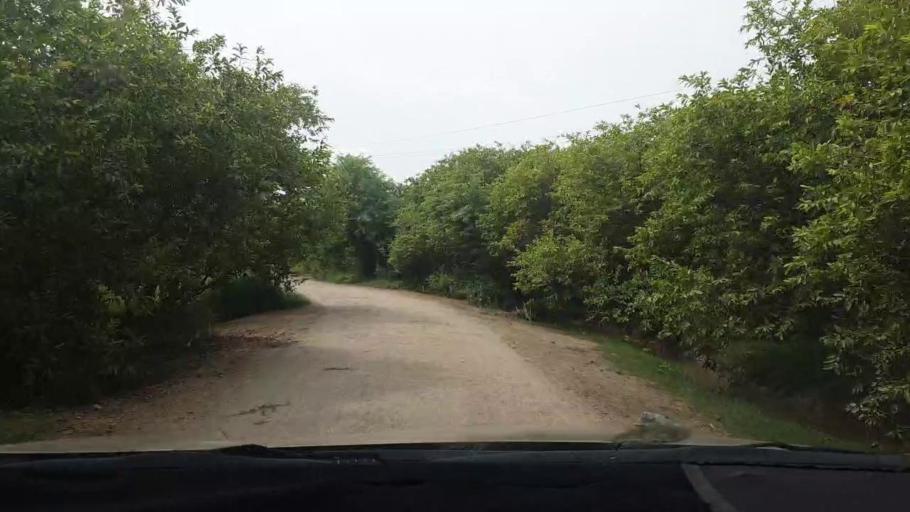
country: PK
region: Sindh
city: Naudero
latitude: 27.6321
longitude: 68.3094
